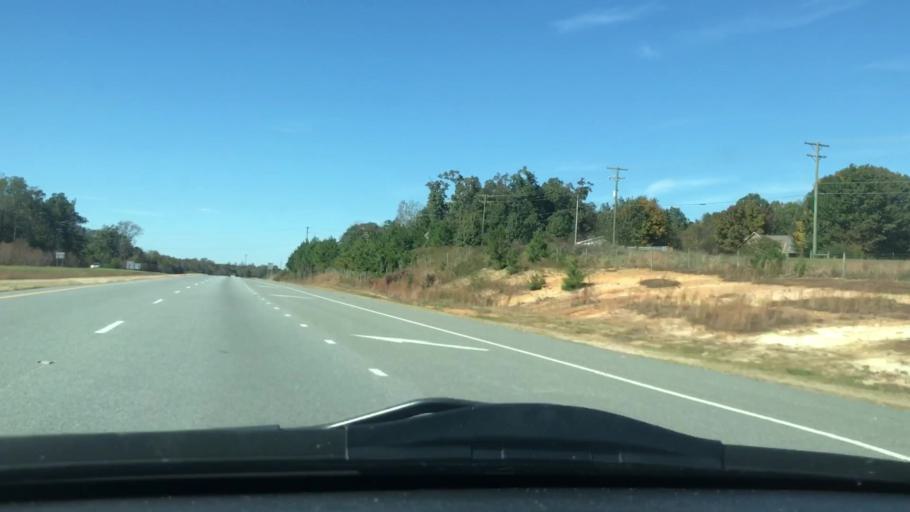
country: US
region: North Carolina
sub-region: Randolph County
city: Archdale
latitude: 35.8753
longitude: -79.9036
